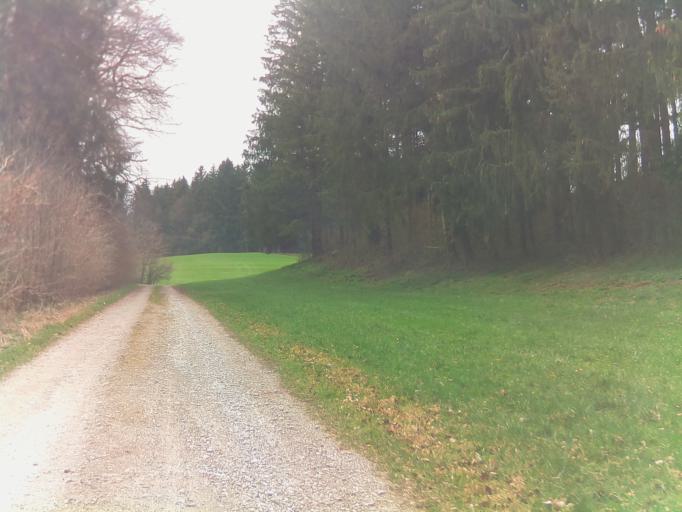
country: DE
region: Bavaria
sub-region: Upper Bavaria
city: Weilheim
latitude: 47.8160
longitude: 11.1845
